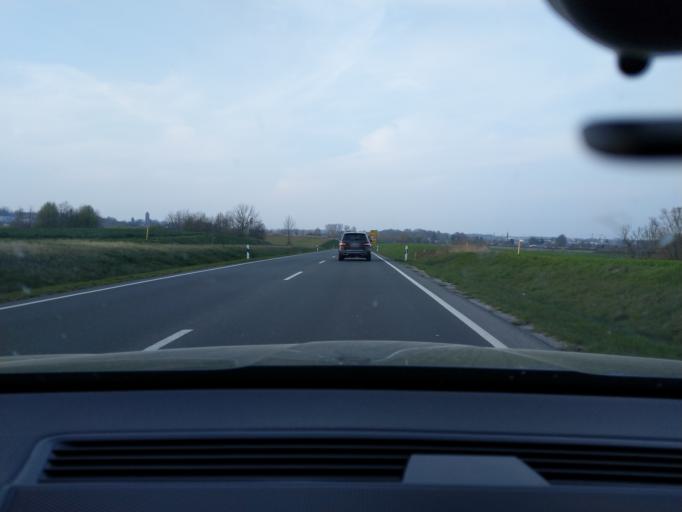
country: DE
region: Mecklenburg-Vorpommern
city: Stralsund
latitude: 54.2906
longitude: 13.0506
